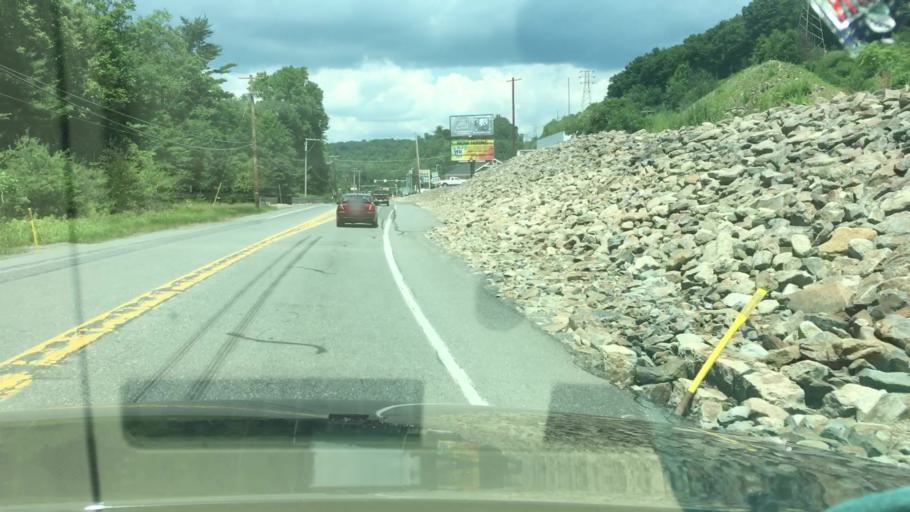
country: US
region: Pennsylvania
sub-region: Schuylkill County
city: Minersville
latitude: 40.6687
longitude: -76.2358
